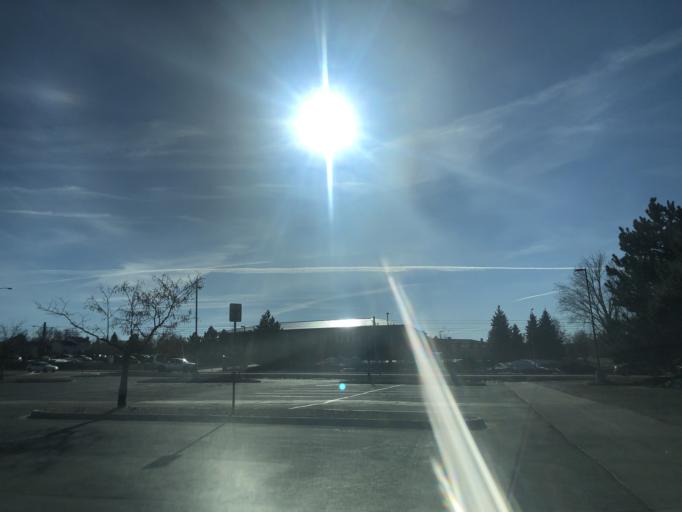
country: US
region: Colorado
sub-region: Adams County
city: Aurora
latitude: 39.7046
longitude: -104.8211
